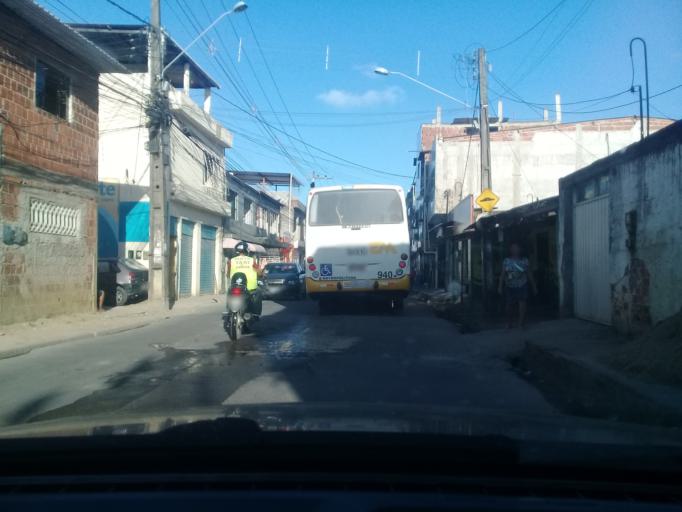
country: BR
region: Pernambuco
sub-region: Jaboatao Dos Guararapes
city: Jaboatao dos Guararapes
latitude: -8.1110
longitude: -34.9588
